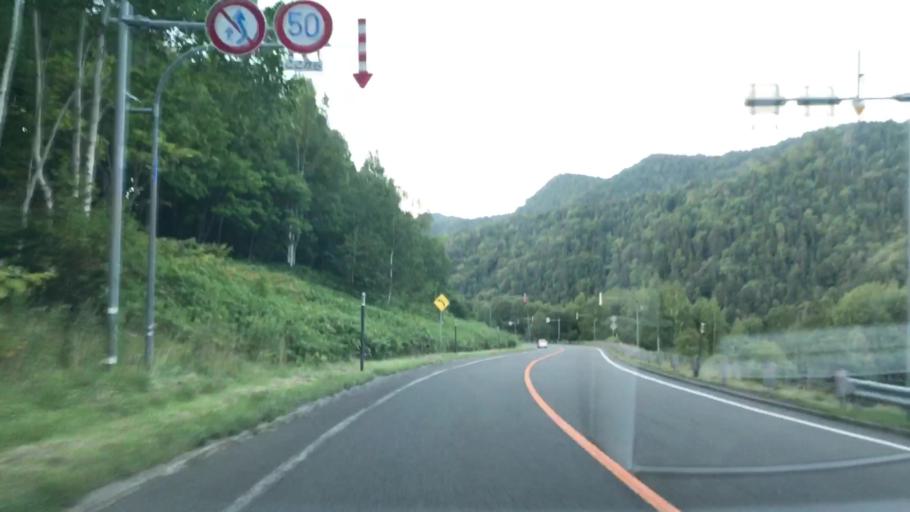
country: JP
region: Hokkaido
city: Sapporo
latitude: 42.9037
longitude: 141.1191
